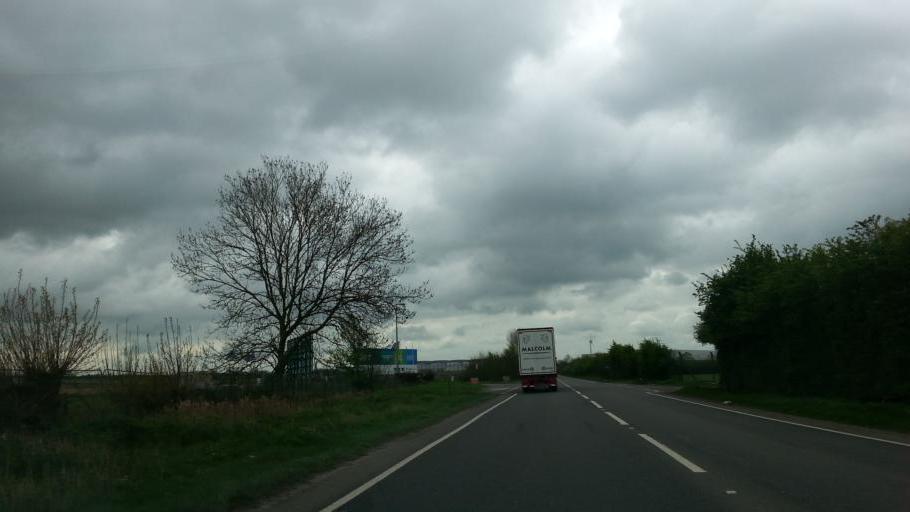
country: GB
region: England
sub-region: Warwickshire
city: Rugby
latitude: 52.3703
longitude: -1.1799
